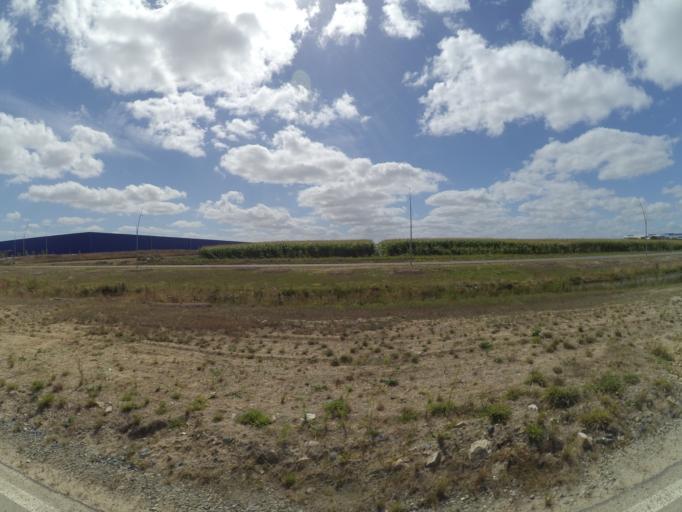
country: FR
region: Pays de la Loire
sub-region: Departement de la Vendee
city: Saint-Hilaire-de-Loulay
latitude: 47.0229
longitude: -1.3514
